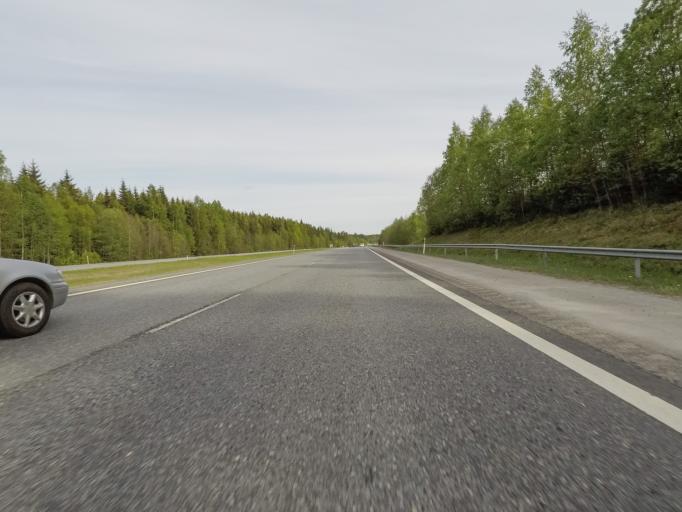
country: FI
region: Haeme
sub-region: Haemeenlinna
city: Tervakoski
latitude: 60.8337
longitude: 24.6525
